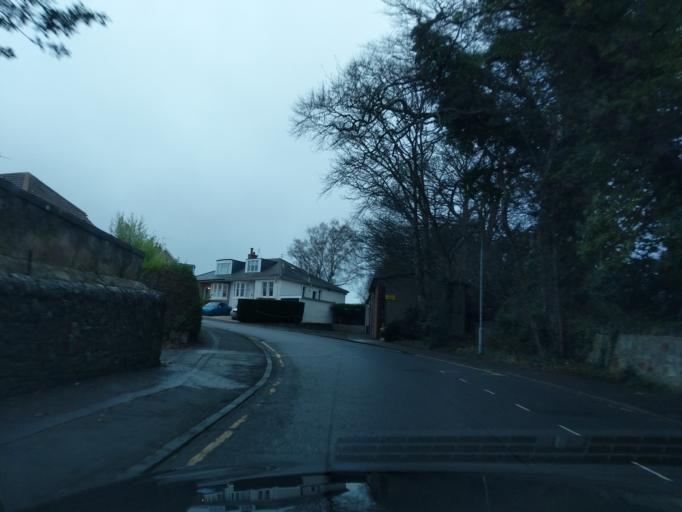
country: GB
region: Scotland
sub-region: Edinburgh
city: Edinburgh
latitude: 55.9577
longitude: -3.2341
